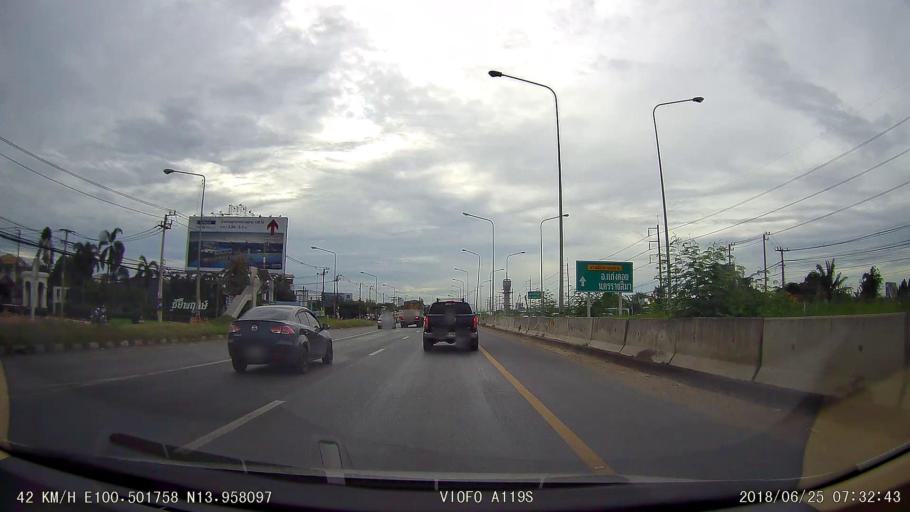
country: TH
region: Nonthaburi
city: Pak Kret
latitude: 13.9581
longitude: 100.5019
